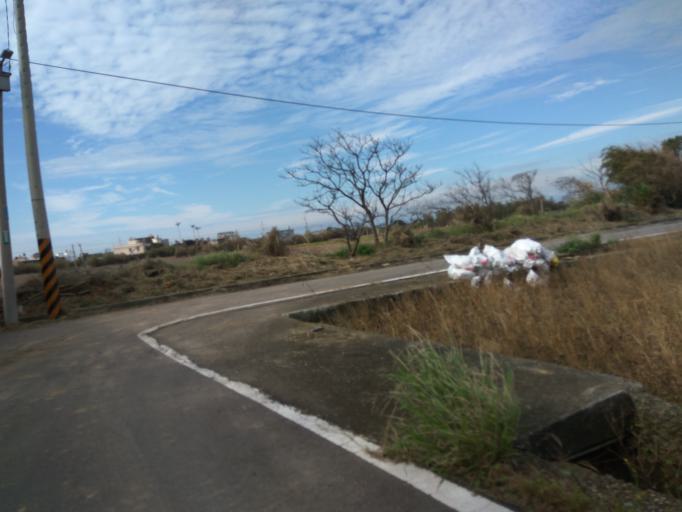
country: TW
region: Taiwan
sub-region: Hsinchu
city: Zhubei
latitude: 25.0093
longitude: 121.0727
